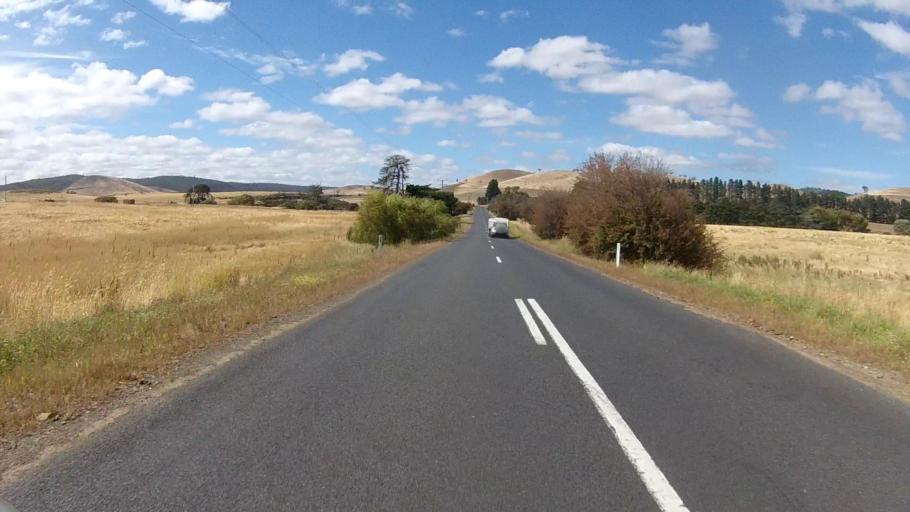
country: AU
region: Tasmania
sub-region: Brighton
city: Bridgewater
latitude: -42.5446
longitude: 147.3734
